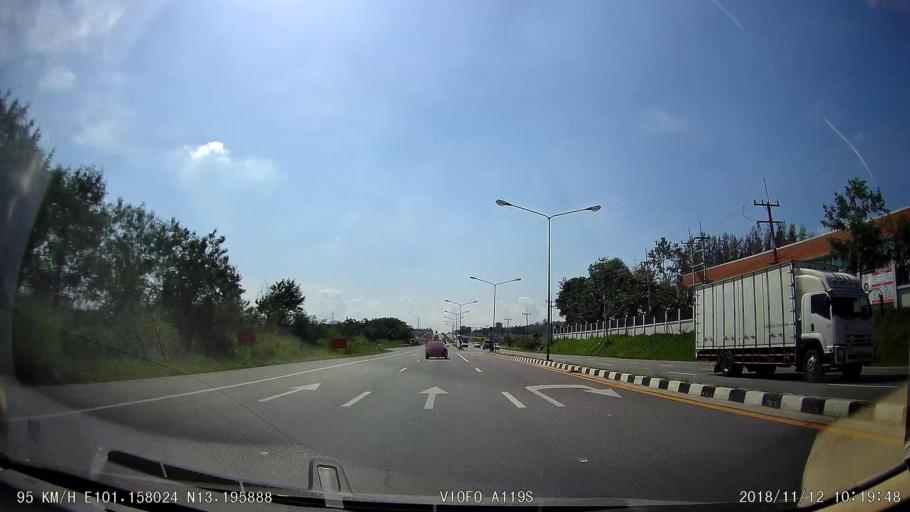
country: TH
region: Chon Buri
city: Ban Bueng
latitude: 13.1954
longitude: 101.1581
